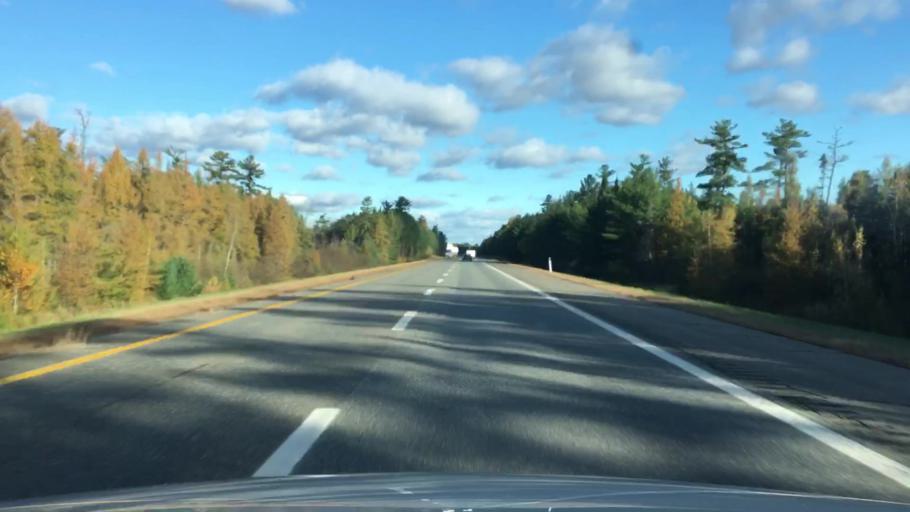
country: US
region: Maine
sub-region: Penobscot County
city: Greenbush
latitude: 45.1334
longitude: -68.6978
